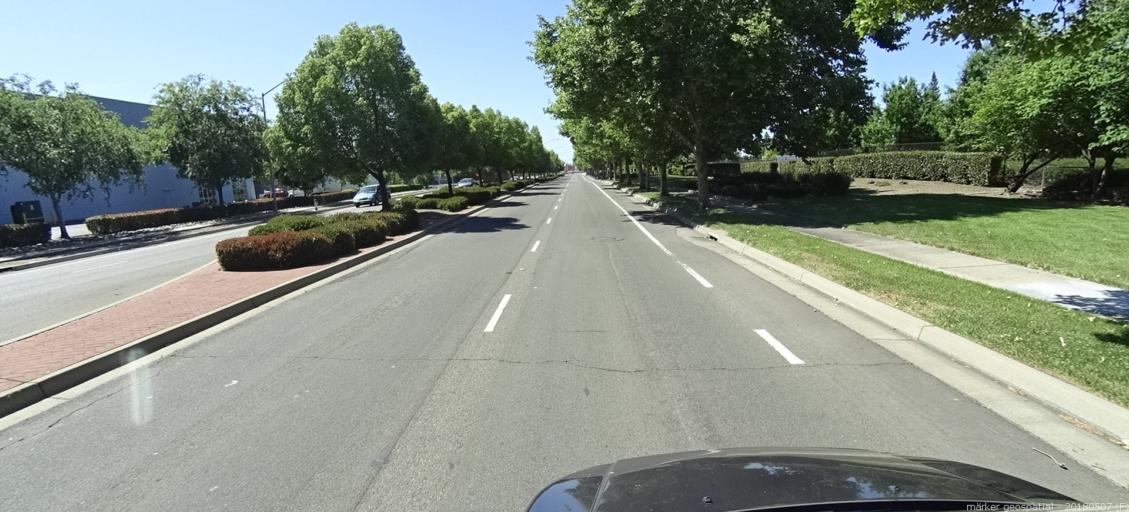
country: US
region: California
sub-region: Sacramento County
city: Sacramento
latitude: 38.6446
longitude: -121.5028
